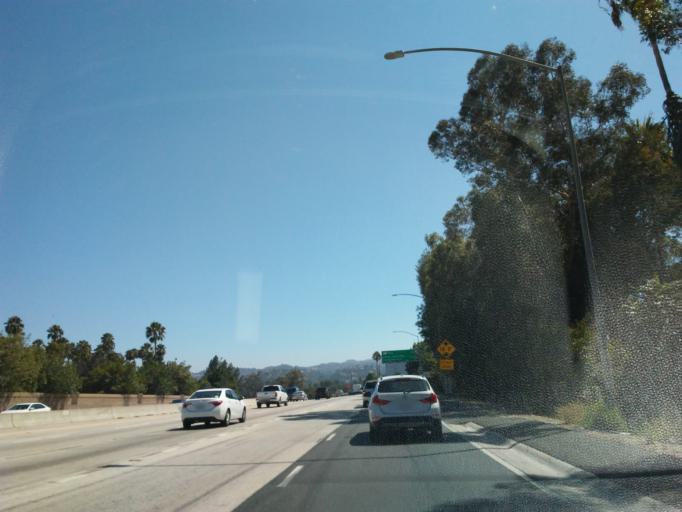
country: US
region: California
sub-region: Los Angeles County
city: Sherman Oaks
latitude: 34.1688
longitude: -118.4686
